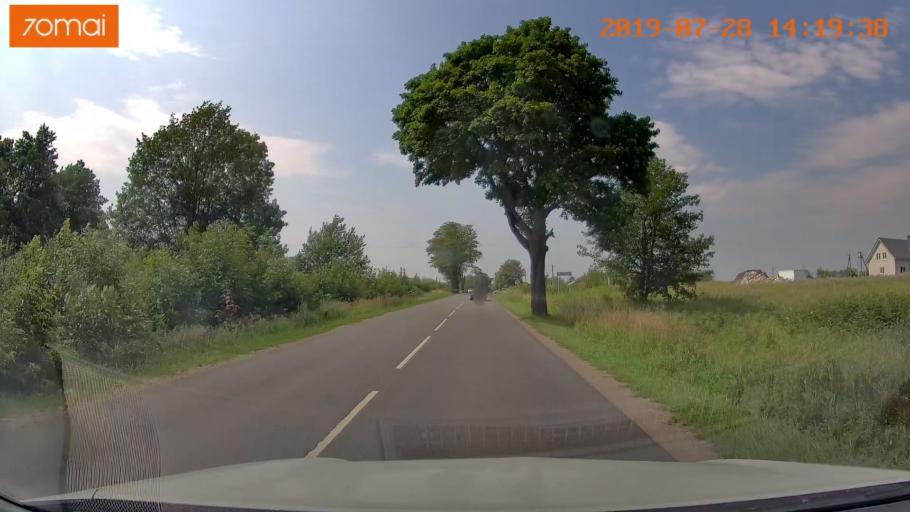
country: RU
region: Kaliningrad
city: Volochayevskoye
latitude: 54.8193
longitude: 20.2220
